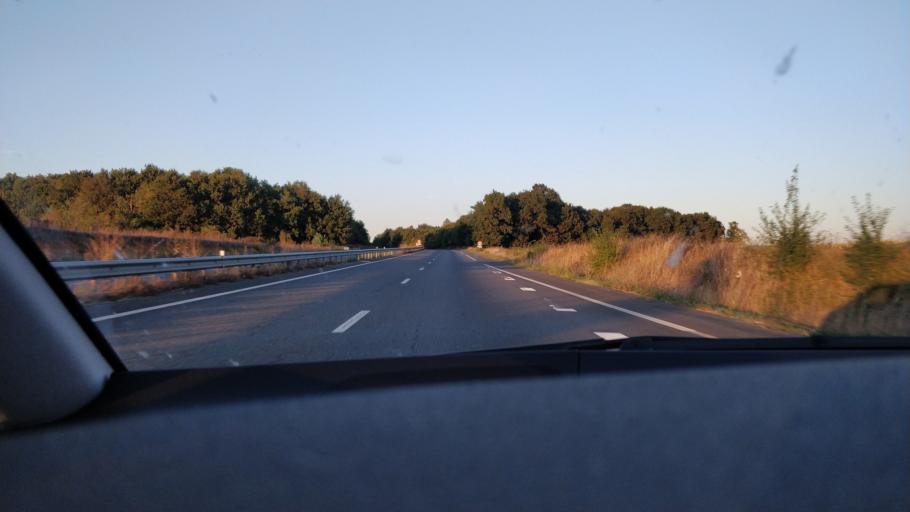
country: FR
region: Poitou-Charentes
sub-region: Departement de la Charente
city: Taponnat-Fleurignac
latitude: 45.7919
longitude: 0.4242
